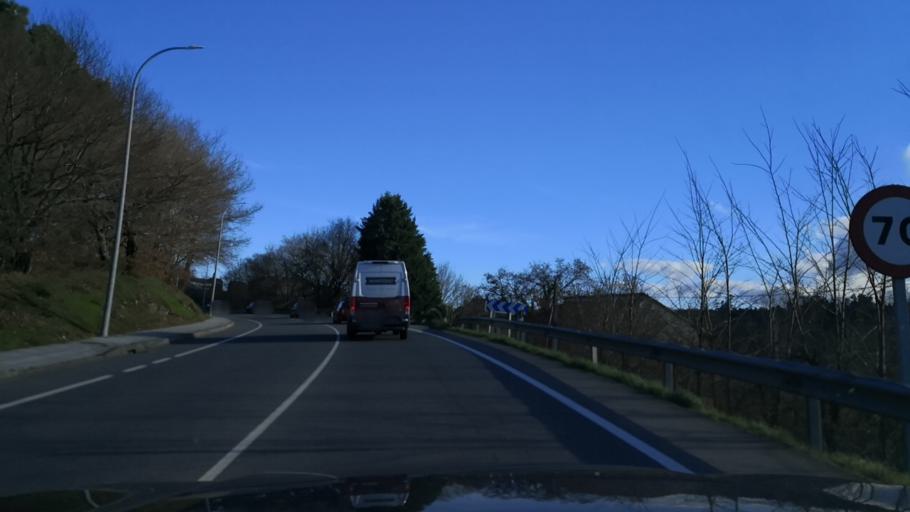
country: ES
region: Galicia
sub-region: Provincia de Pontevedra
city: Silleda
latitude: 42.6999
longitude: -8.2543
